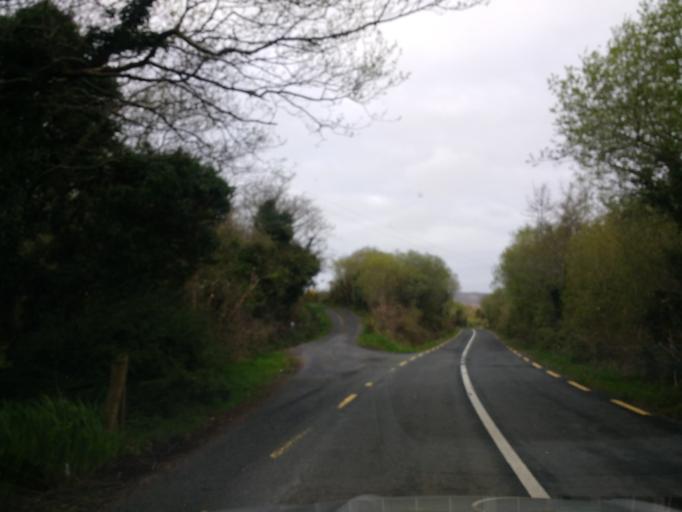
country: IE
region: Ulster
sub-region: County Donegal
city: Buncrana
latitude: 55.1579
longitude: -7.5633
